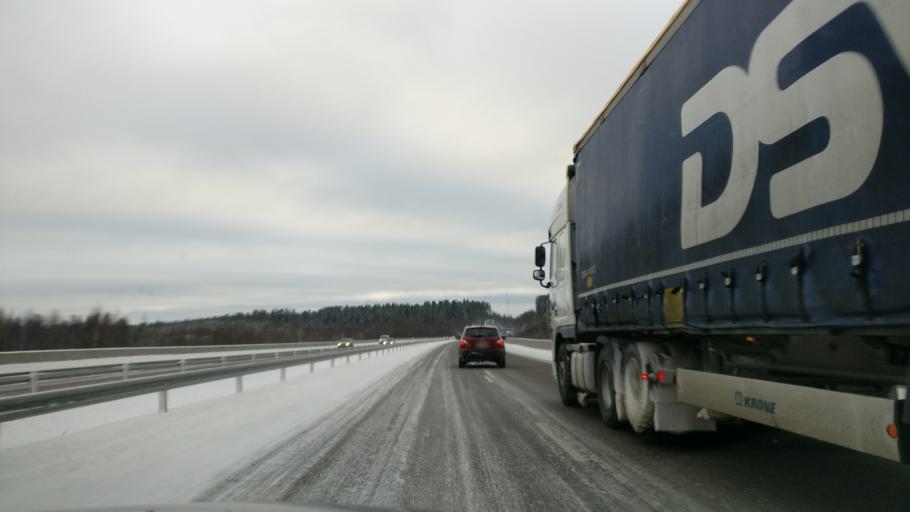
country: FI
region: Paijanne Tavastia
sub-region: Lahti
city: Nastola
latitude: 61.0091
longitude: 25.8148
